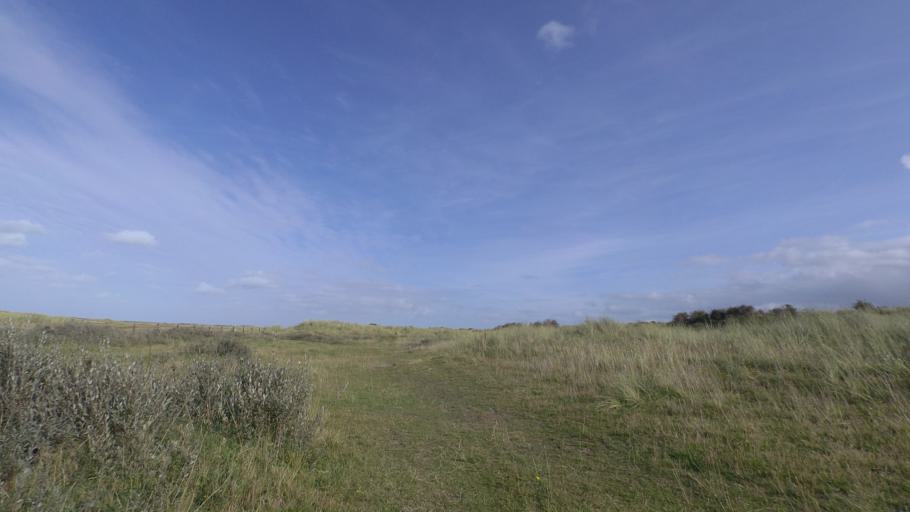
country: NL
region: Friesland
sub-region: Gemeente Ameland
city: Nes
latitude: 53.4528
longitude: 5.8449
